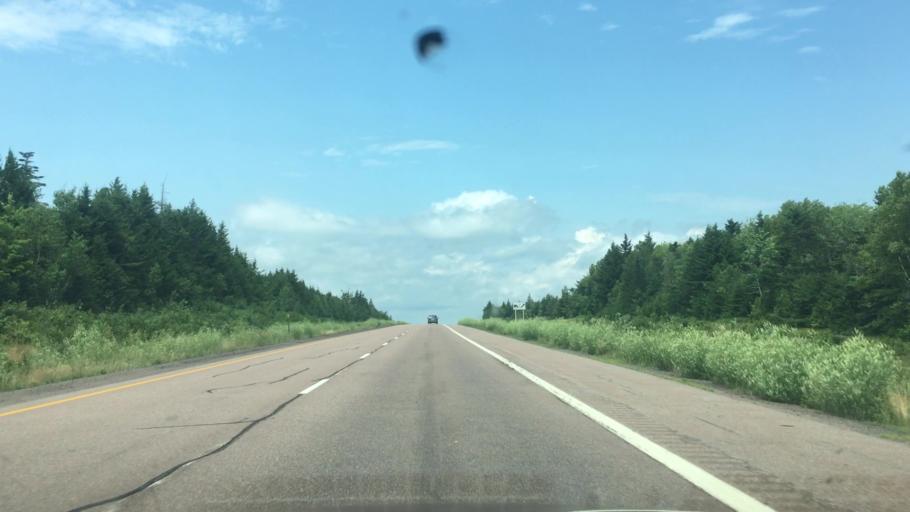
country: CA
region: New Brunswick
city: Sackville
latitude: 45.9559
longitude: -64.4116
